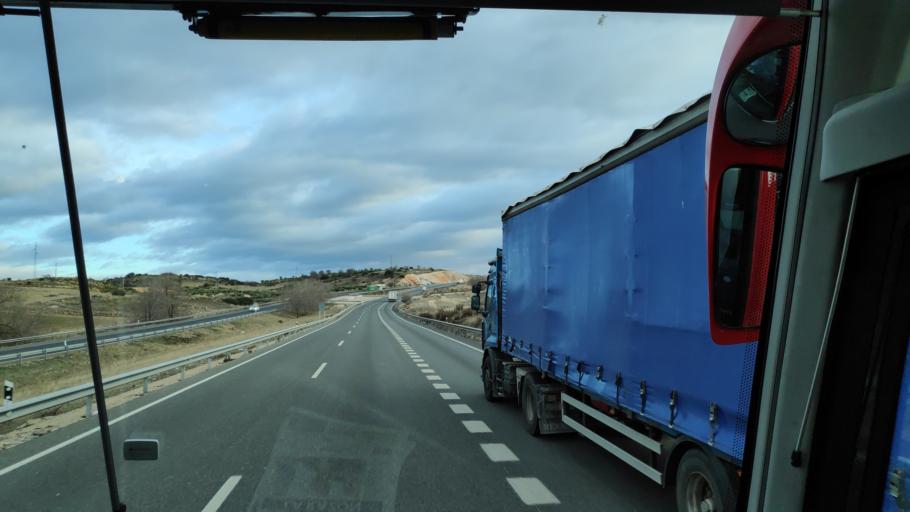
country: ES
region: Madrid
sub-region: Provincia de Madrid
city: Villarejo de Salvanes
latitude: 40.1957
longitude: -3.3053
